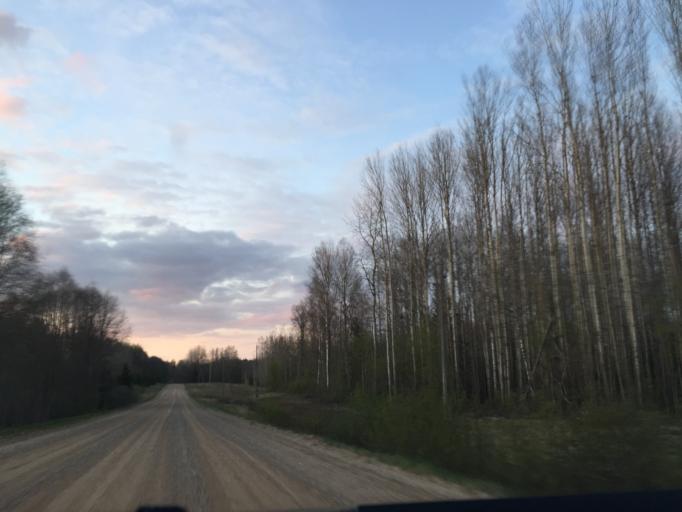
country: LV
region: Aluksnes Rajons
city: Aluksne
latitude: 57.3764
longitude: 27.0268
